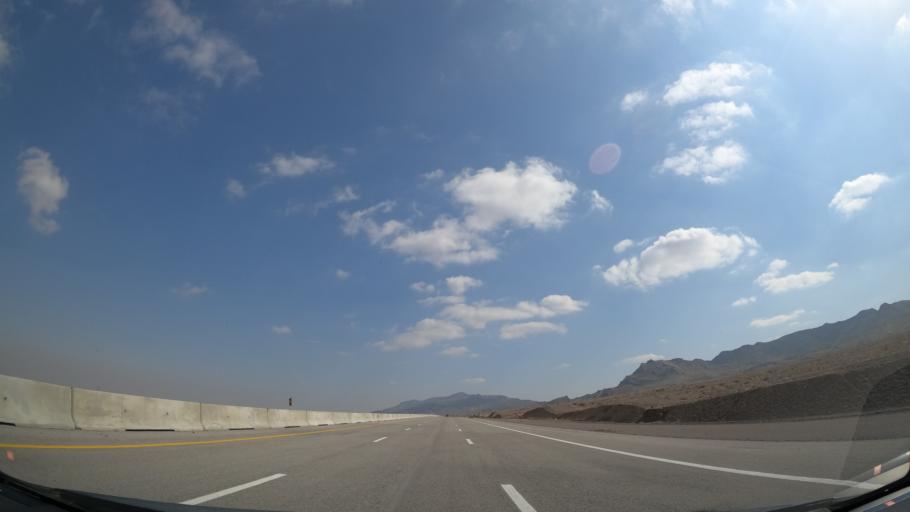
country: IR
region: Alborz
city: Eshtehard
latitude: 35.7088
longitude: 50.6013
